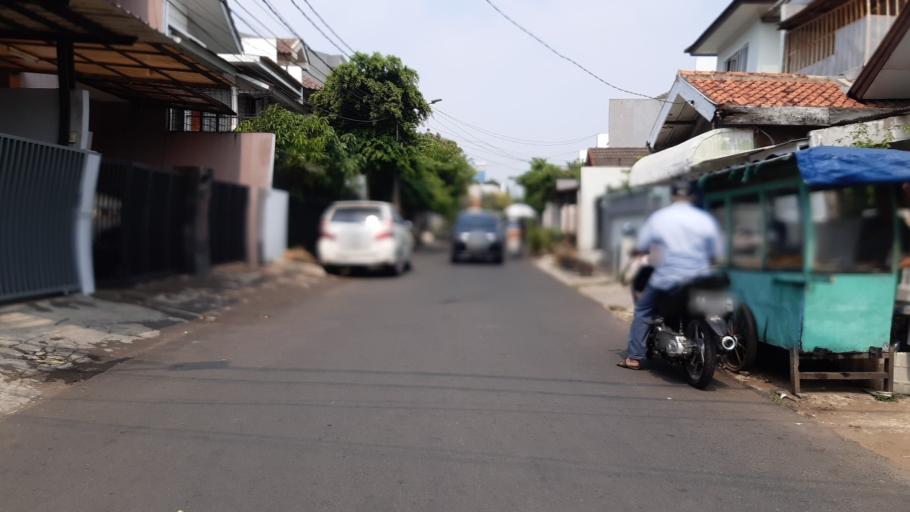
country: ID
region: Jakarta Raya
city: Jakarta
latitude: -6.2367
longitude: 106.8574
